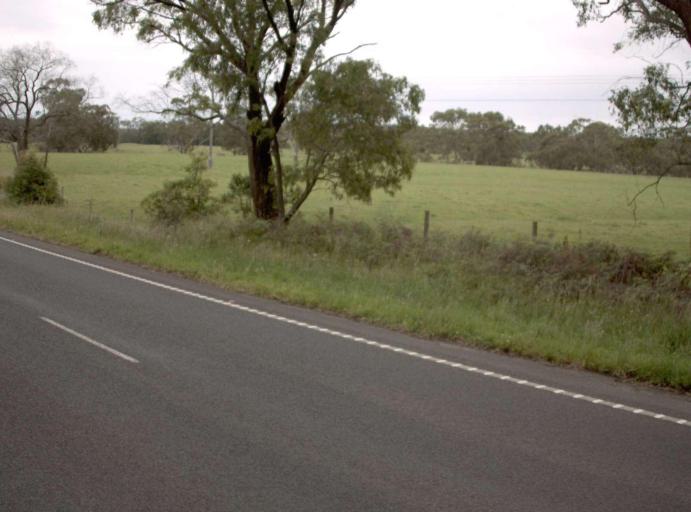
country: AU
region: Victoria
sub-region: Bass Coast
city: North Wonthaggi
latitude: -38.5684
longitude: 145.9731
